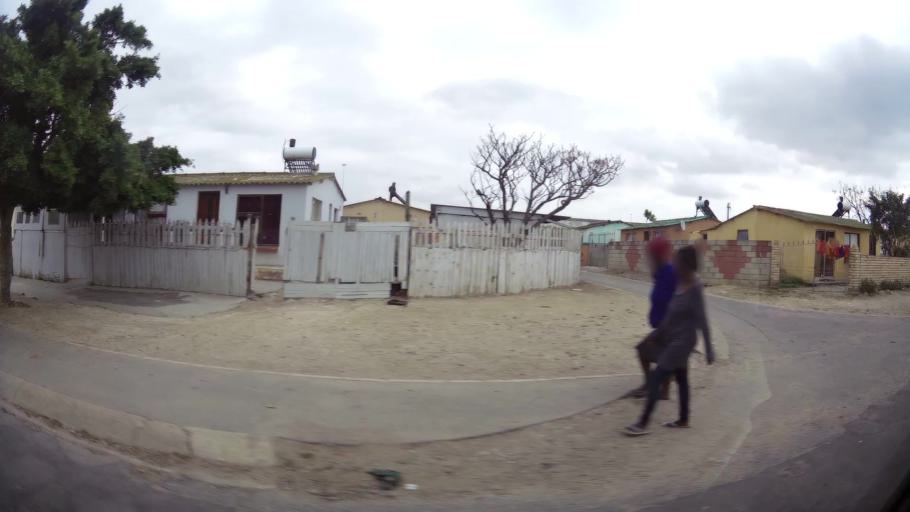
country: ZA
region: Eastern Cape
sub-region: Nelson Mandela Bay Metropolitan Municipality
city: Port Elizabeth
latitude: -33.8788
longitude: 25.5965
